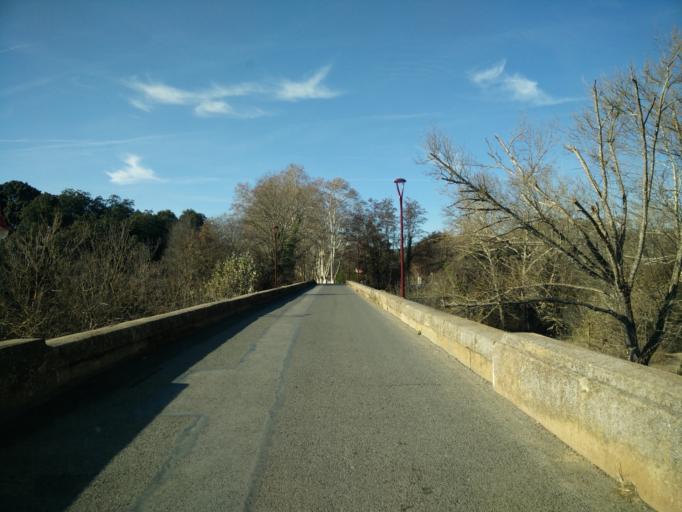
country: FR
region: Provence-Alpes-Cote d'Azur
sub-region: Departement du Var
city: Vidauban
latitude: 43.4283
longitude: 6.4288
